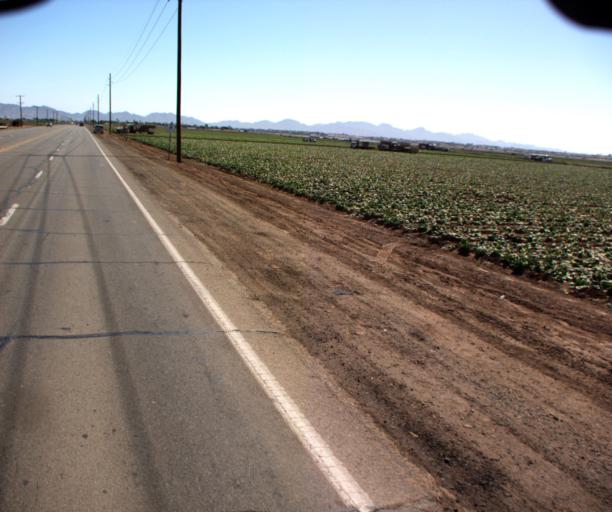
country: US
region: Arizona
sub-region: Yuma County
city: Yuma
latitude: 32.6988
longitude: -114.5623
